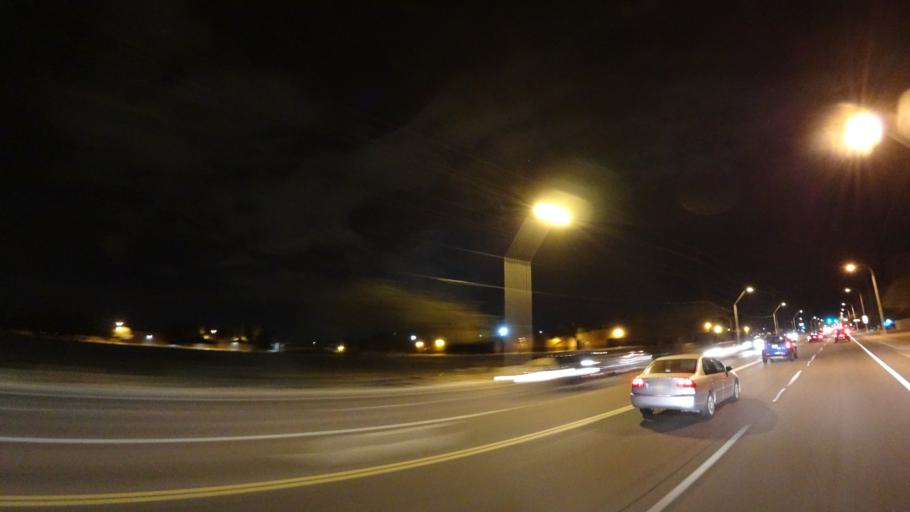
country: US
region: Arizona
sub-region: Maricopa County
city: San Carlos
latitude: 33.3268
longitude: -111.8765
